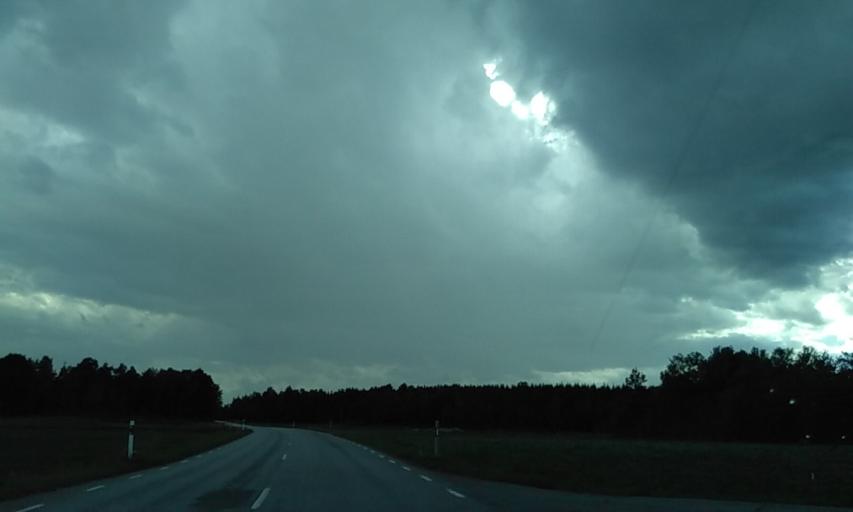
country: SE
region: Vaestra Goetaland
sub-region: Lidkopings Kommun
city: Lidkoping
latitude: 58.5051
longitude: 12.9916
